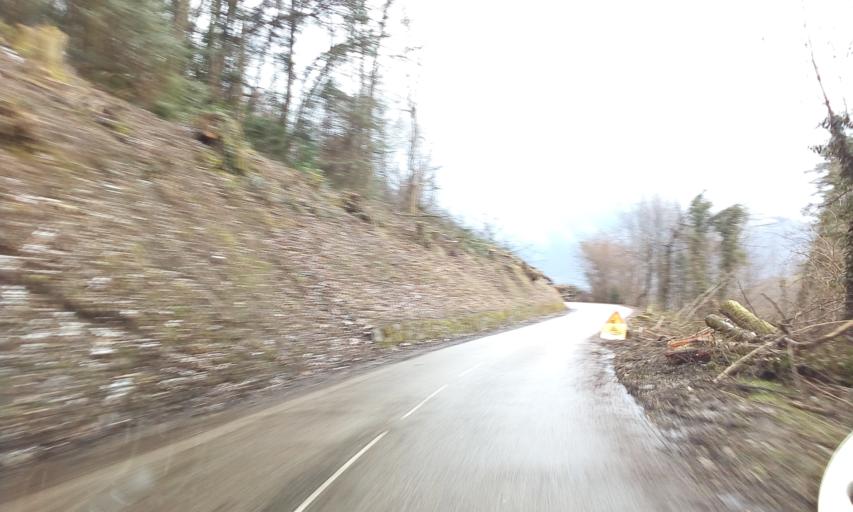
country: FR
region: Rhone-Alpes
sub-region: Departement de l'Isere
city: Le Versoud
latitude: 45.2072
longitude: 5.8766
